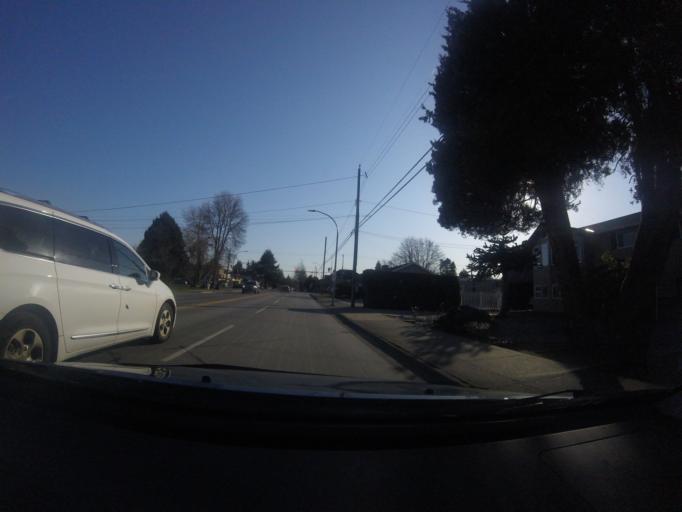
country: CA
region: British Columbia
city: Richmond
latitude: 49.1490
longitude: -123.1251
